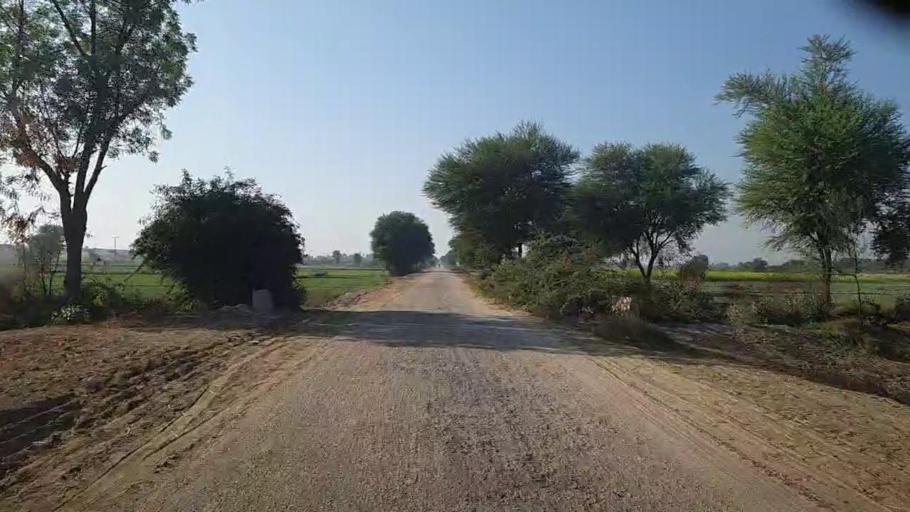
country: PK
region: Sindh
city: Darya Khan Marri
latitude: 26.6825
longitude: 68.3626
